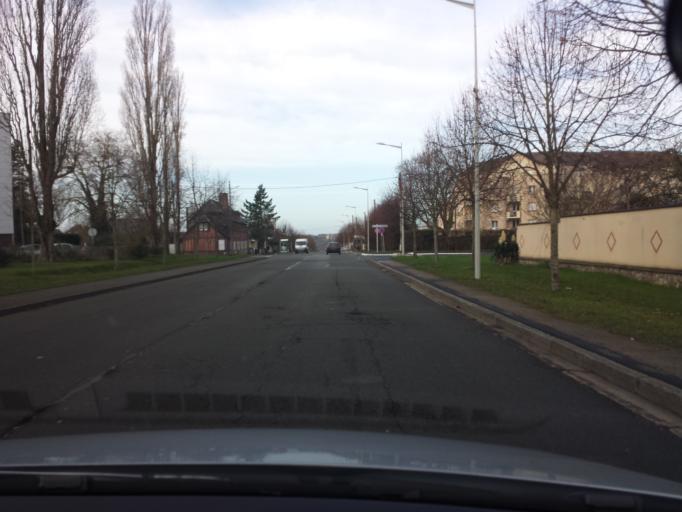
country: FR
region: Haute-Normandie
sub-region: Departement de l'Eure
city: Evreux
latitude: 49.0177
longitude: 1.1684
